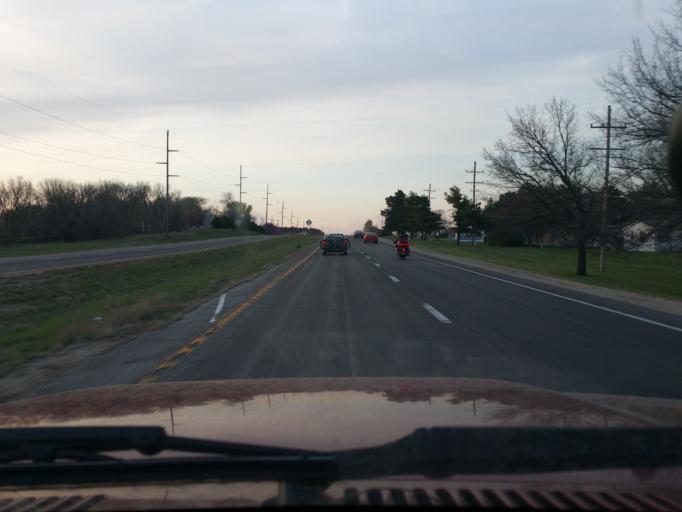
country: US
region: Kansas
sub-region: Riley County
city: Manhattan
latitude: 39.2207
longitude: -96.5798
